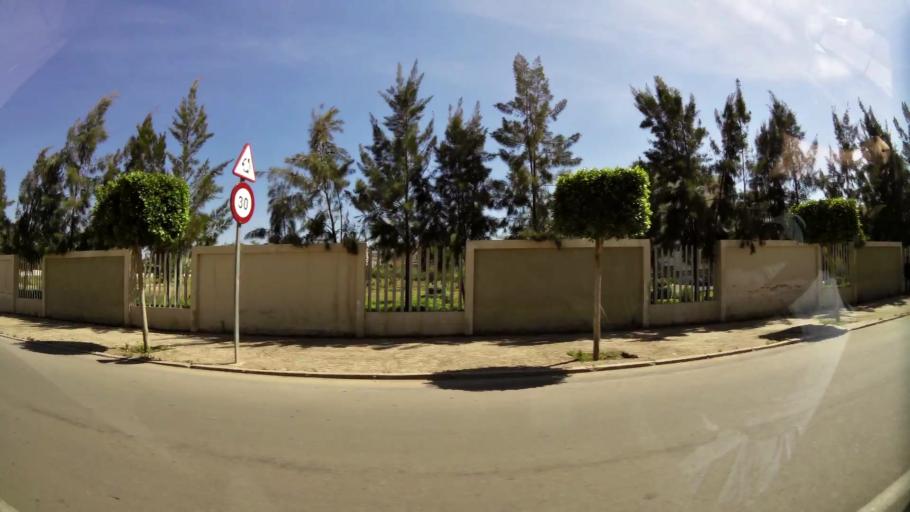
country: MA
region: Oriental
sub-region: Oujda-Angad
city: Oujda
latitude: 34.6572
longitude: -1.9097
